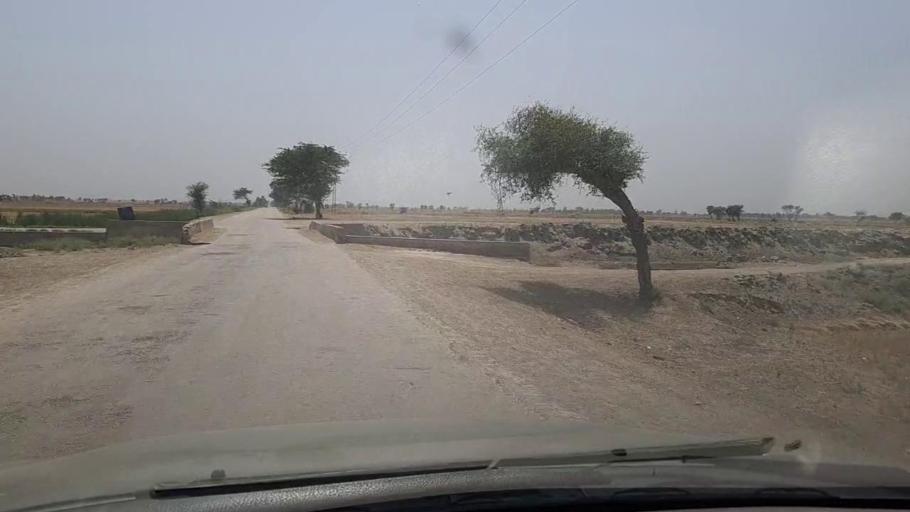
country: PK
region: Sindh
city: Miro Khan
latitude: 27.7086
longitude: 68.0640
